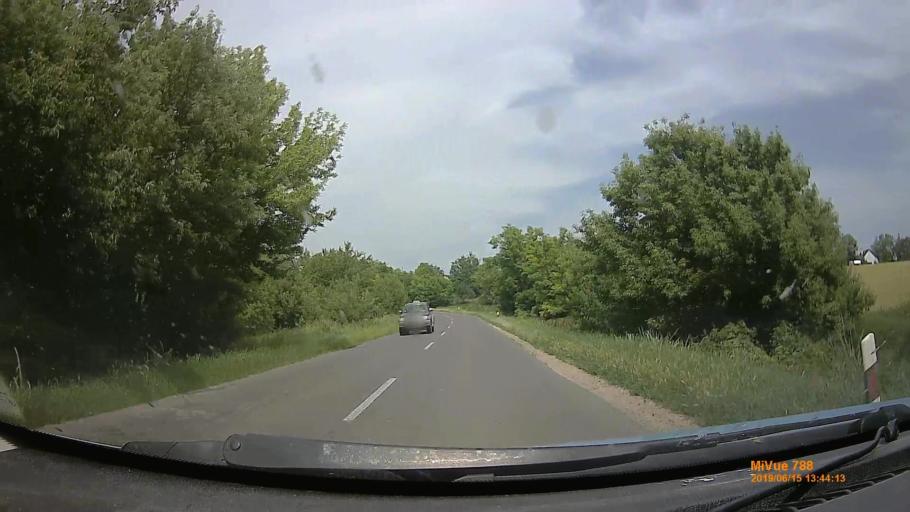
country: HU
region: Tolna
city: Iregszemcse
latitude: 46.6857
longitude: 18.1894
